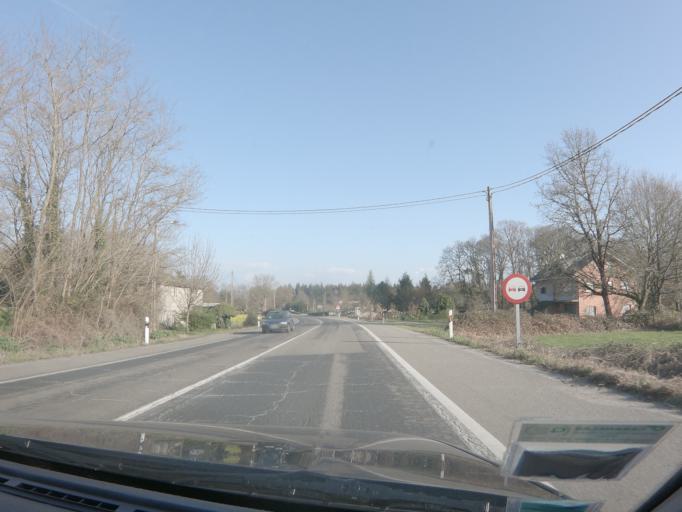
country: ES
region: Galicia
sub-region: Provincia de Lugo
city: Corgo
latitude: 42.9532
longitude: -7.4624
